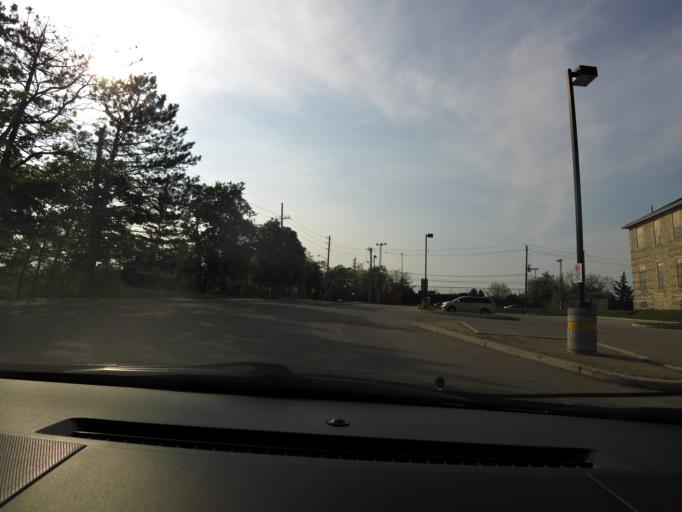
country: CA
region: Ontario
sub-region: Wellington County
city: Guelph
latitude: 43.5430
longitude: -80.2524
